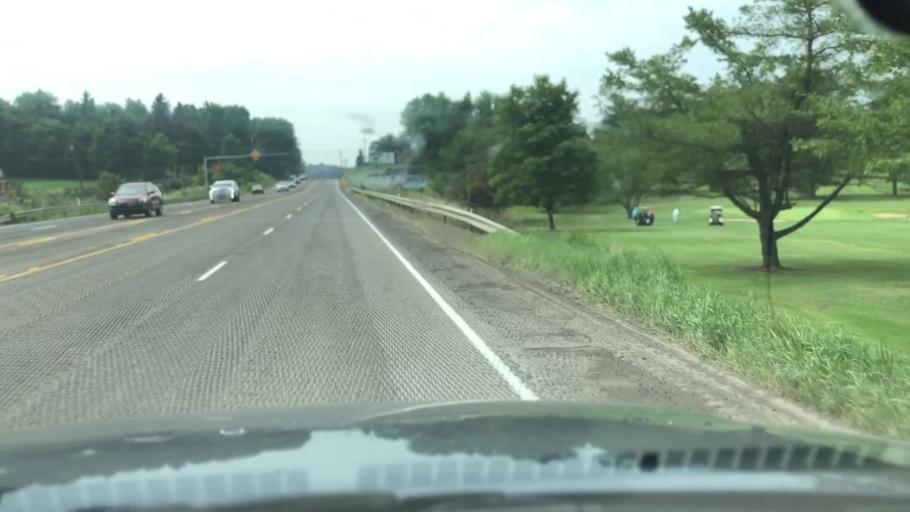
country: US
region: Pennsylvania
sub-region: Butler County
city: Nixon
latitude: 40.7537
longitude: -79.9246
